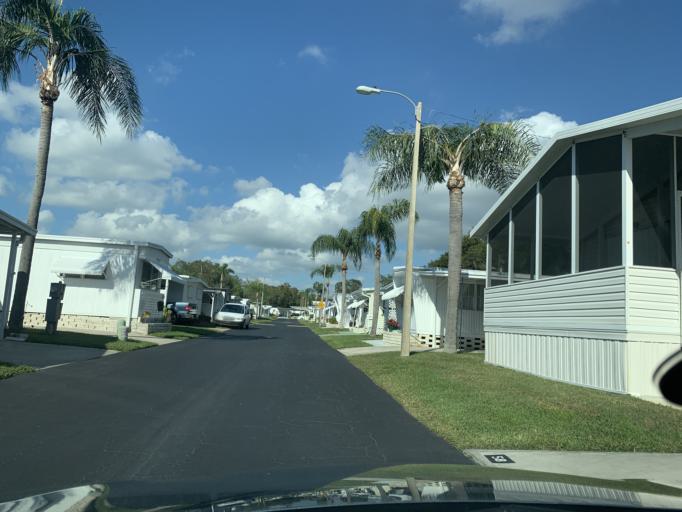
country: US
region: Florida
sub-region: Pinellas County
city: Largo
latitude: 27.9251
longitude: -82.7923
